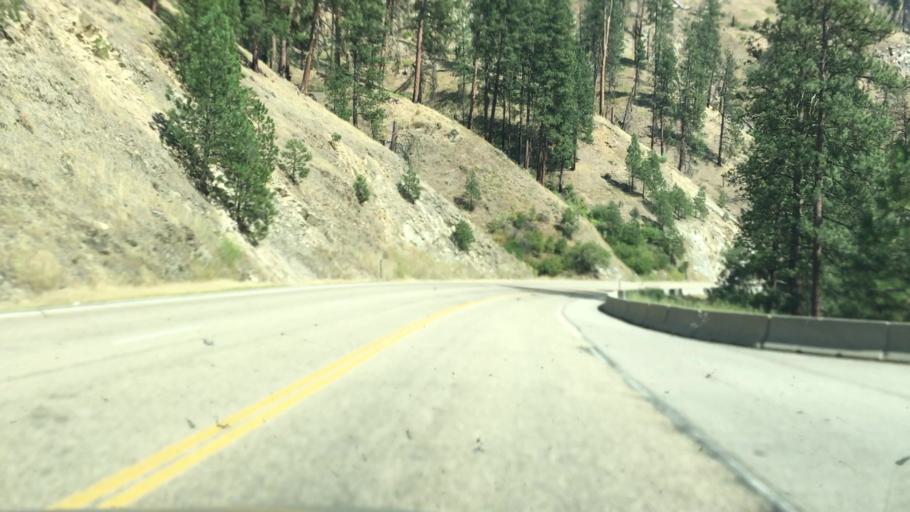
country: US
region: Idaho
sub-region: Boise County
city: Idaho City
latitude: 44.1084
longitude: -116.0972
